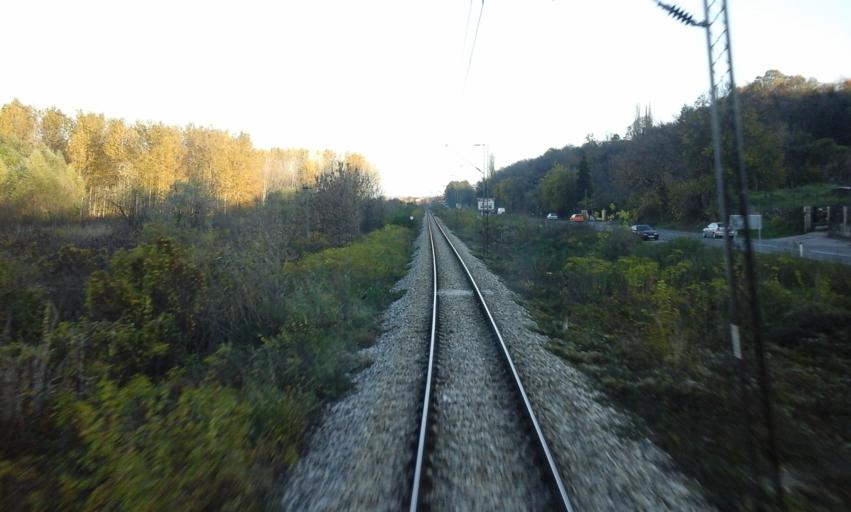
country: RS
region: Autonomna Pokrajina Vojvodina
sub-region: Juznobacki Okrug
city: Sremski Karlovci
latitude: 45.2140
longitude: 19.9129
